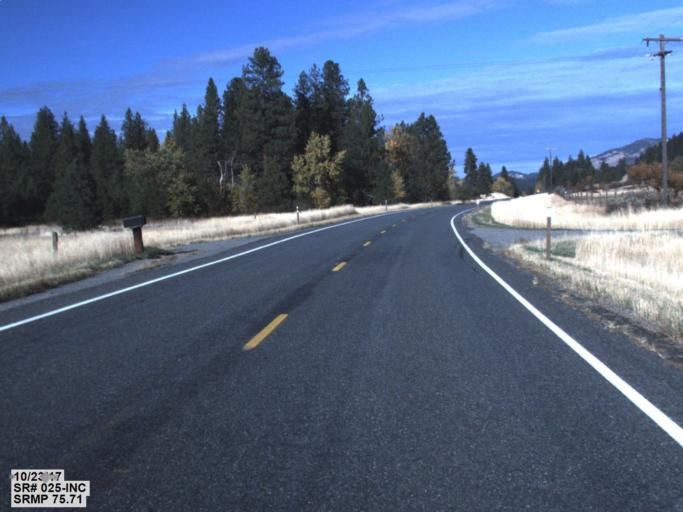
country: US
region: Washington
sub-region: Stevens County
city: Kettle Falls
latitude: 48.5506
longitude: -118.1270
